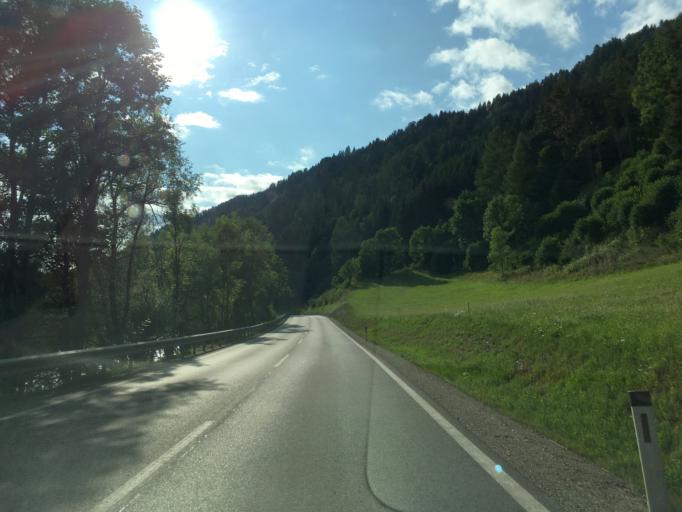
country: AT
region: Styria
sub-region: Politischer Bezirk Murau
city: Murau
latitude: 47.1138
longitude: 14.1542
